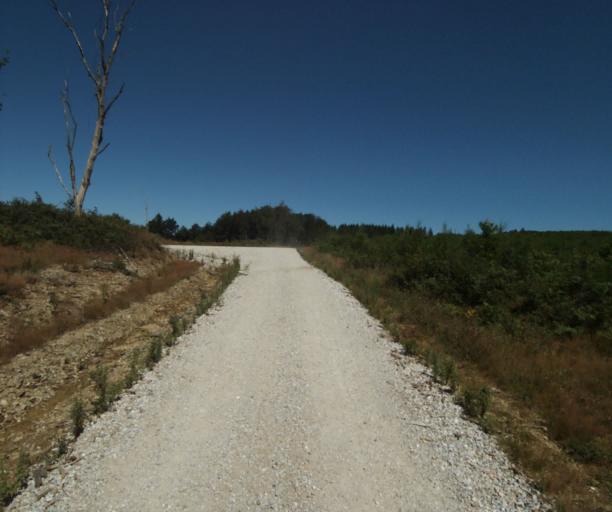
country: FR
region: Midi-Pyrenees
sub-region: Departement du Tarn
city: Dourgne
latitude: 43.4406
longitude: 2.1176
